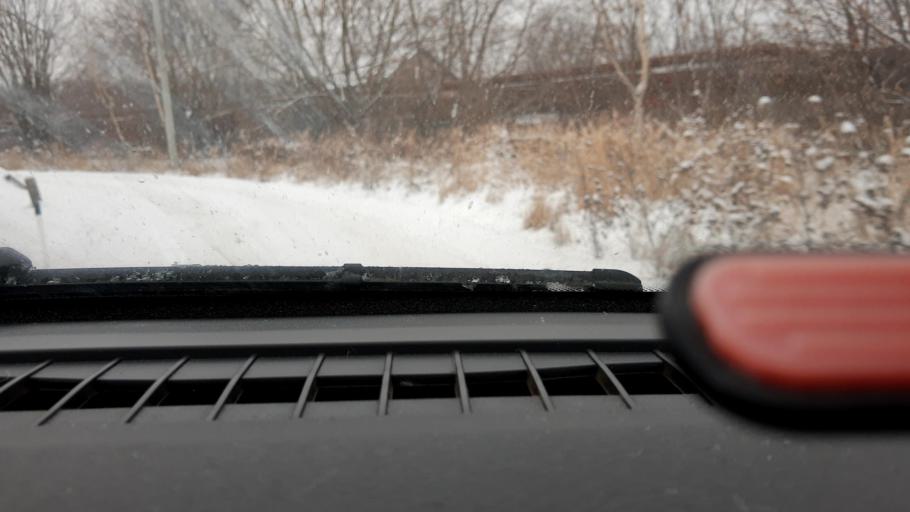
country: RU
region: Nizjnij Novgorod
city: Novaya Balakhna
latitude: 56.5169
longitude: 43.5721
